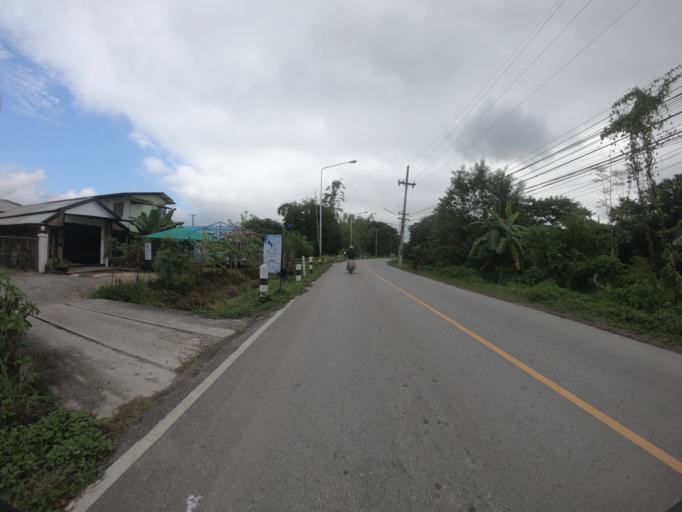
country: TH
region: Chiang Mai
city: Hang Dong
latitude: 18.7110
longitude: 98.9429
